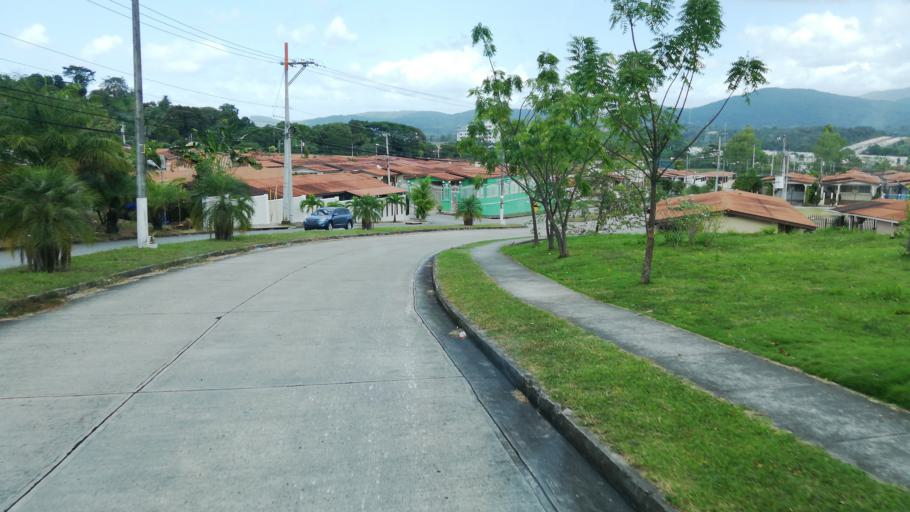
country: PA
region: Panama
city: San Miguelito
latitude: 9.0757
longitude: -79.4576
